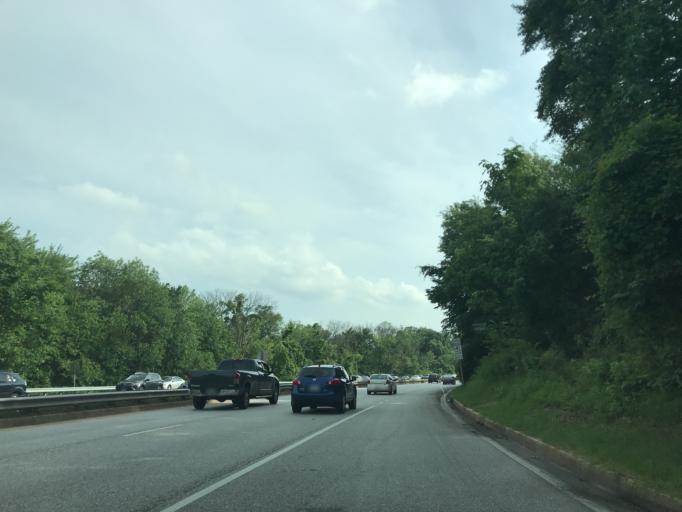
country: US
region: Maryland
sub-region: Baltimore County
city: Parkville
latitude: 39.3885
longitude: -76.5514
